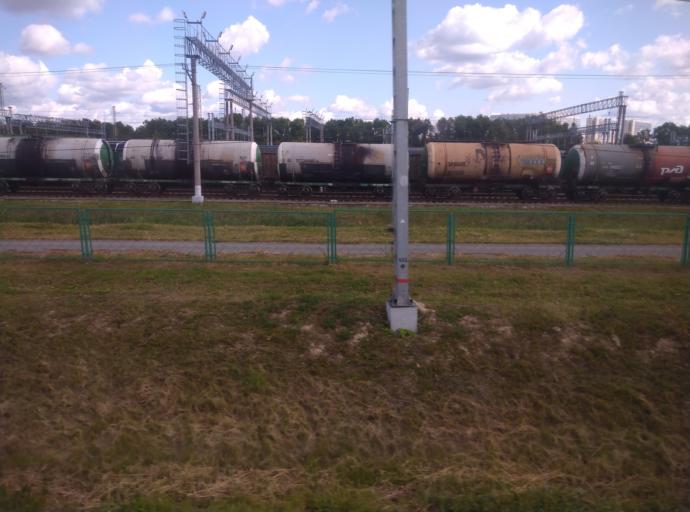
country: RU
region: St.-Petersburg
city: Obukhovo
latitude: 59.8591
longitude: 30.4373
